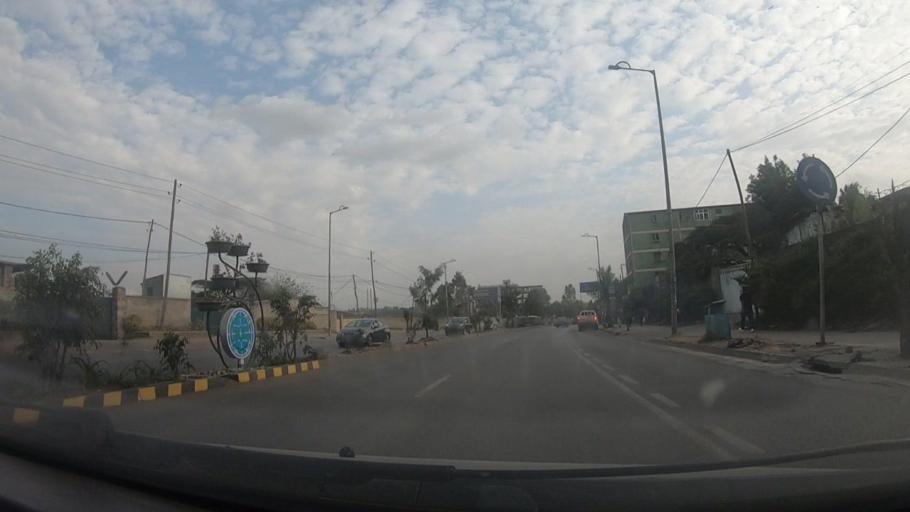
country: ET
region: Adis Abeba
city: Addis Ababa
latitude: 8.9669
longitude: 38.7321
